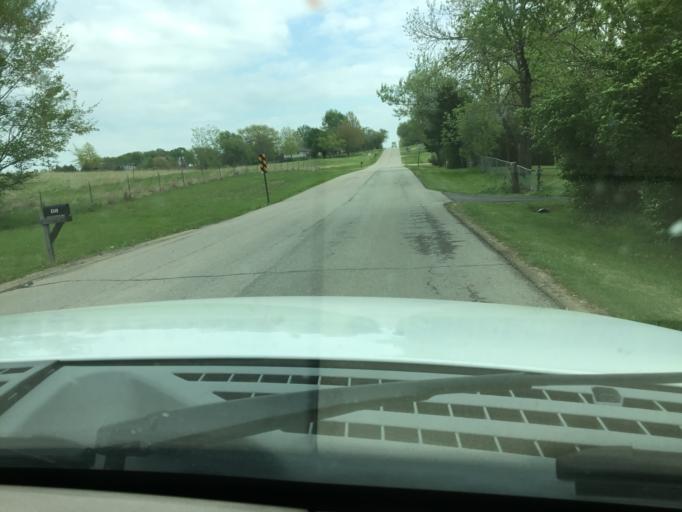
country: US
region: Kansas
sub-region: Shawnee County
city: Auburn
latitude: 38.9709
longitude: -95.8168
